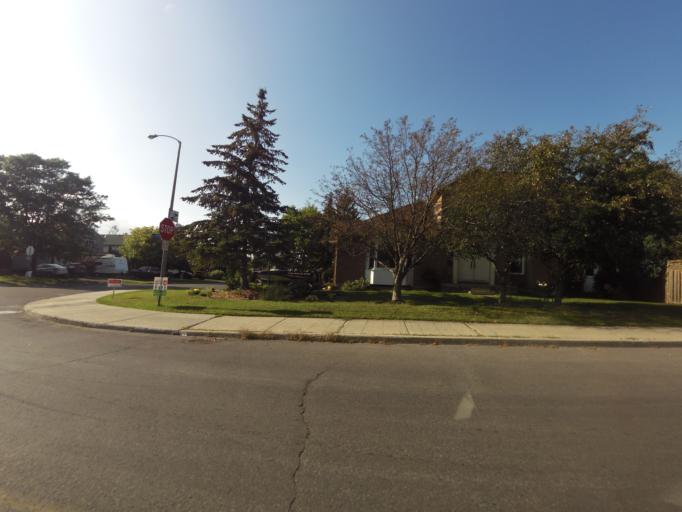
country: CA
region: Ontario
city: Clarence-Rockland
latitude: 45.4841
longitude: -75.4845
